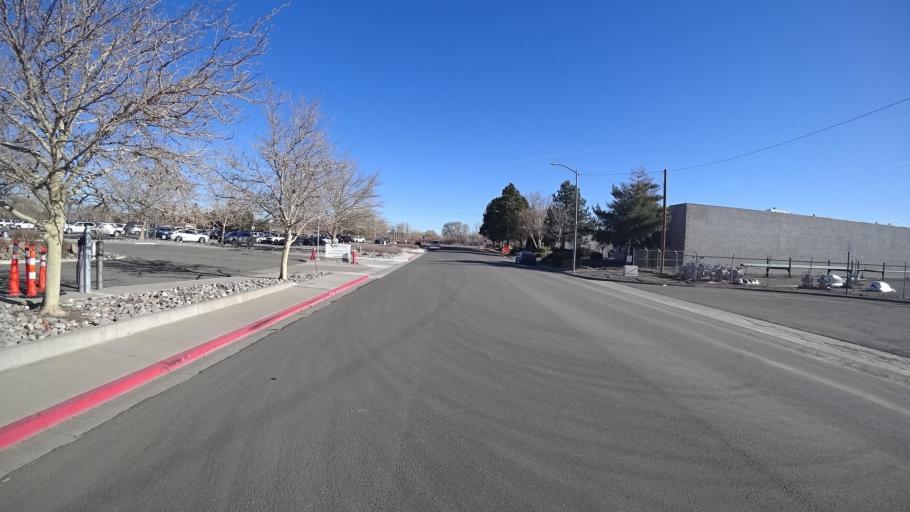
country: US
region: Nevada
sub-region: Washoe County
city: Sparks
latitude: 39.5135
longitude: -119.7560
